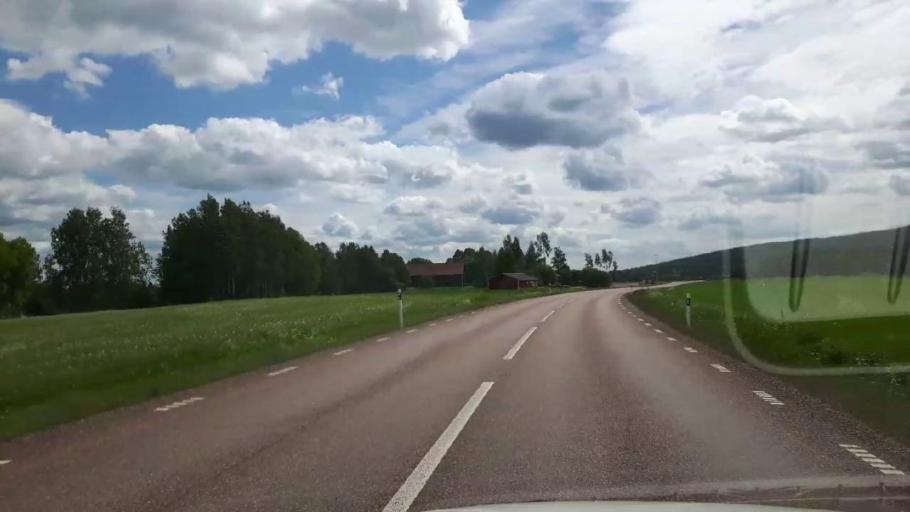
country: SE
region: Dalarna
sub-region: Saters Kommun
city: Saeter
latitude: 60.4050
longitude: 15.8714
